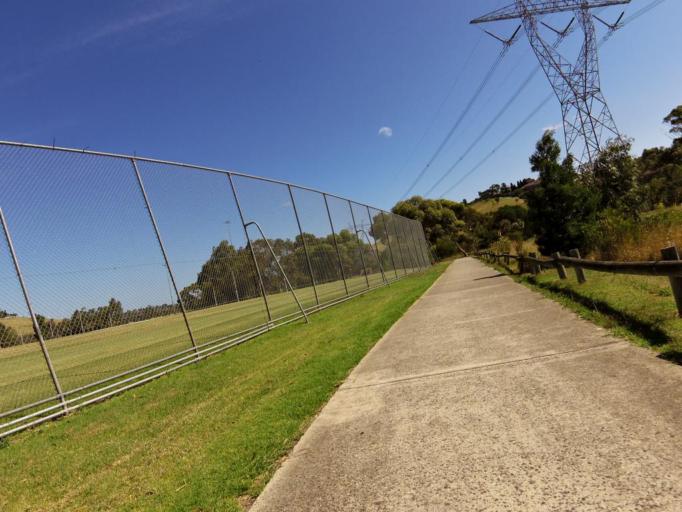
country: AU
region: Victoria
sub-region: Hume
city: Jacana
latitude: -37.6814
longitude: 144.9036
